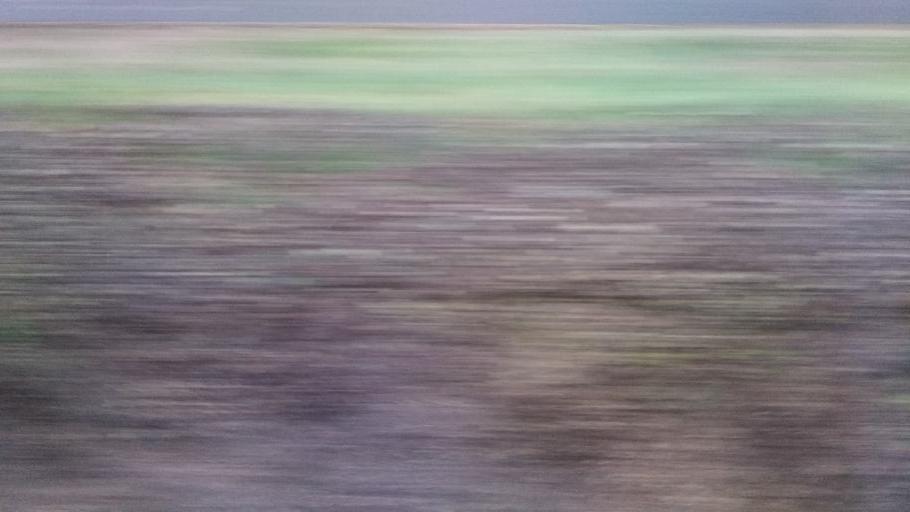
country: AT
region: Vorarlberg
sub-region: Politischer Bezirk Bregenz
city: Wolfurt
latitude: 47.4686
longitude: 9.7376
